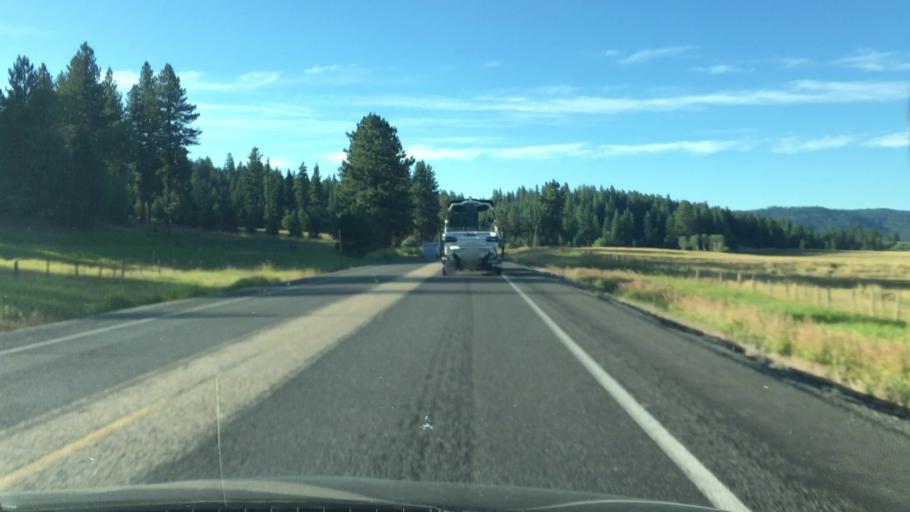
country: US
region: Idaho
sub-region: Valley County
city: Cascade
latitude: 44.5554
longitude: -116.0282
